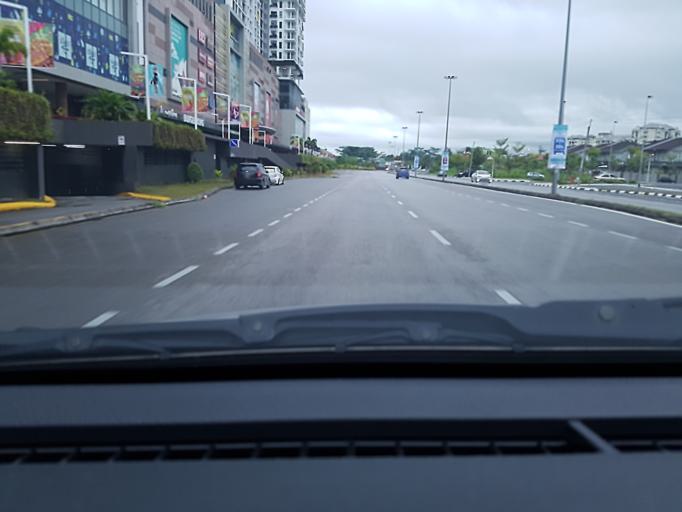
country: MY
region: Sarawak
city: Kuching
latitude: 1.5273
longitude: 110.3704
